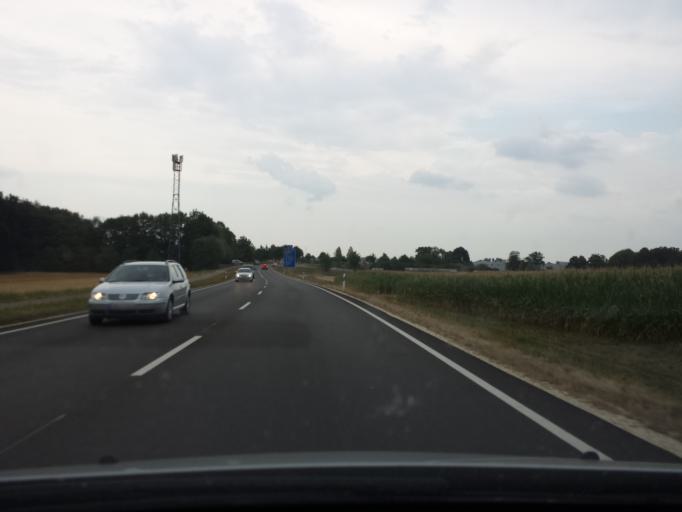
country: DE
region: Bavaria
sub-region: Swabia
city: Leipheim
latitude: 48.4423
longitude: 10.2034
